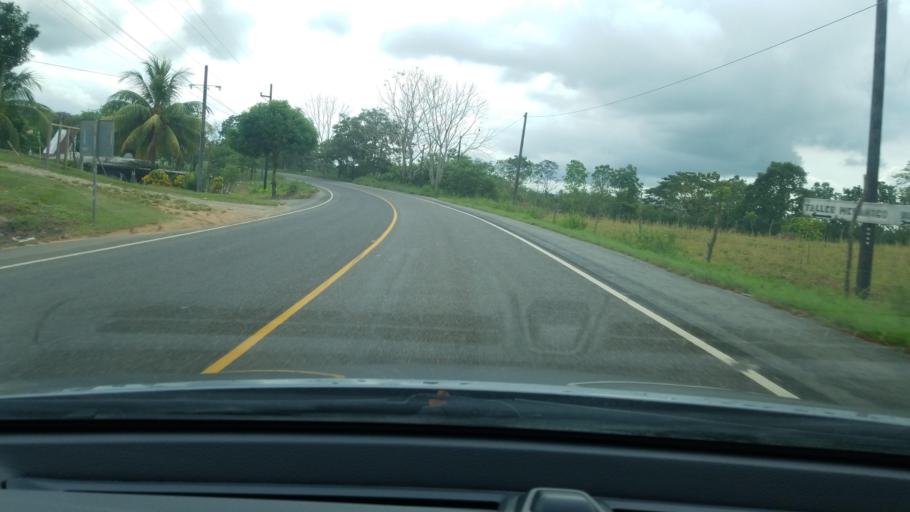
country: HN
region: Cortes
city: Potrerillos
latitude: 15.5962
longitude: -88.3181
